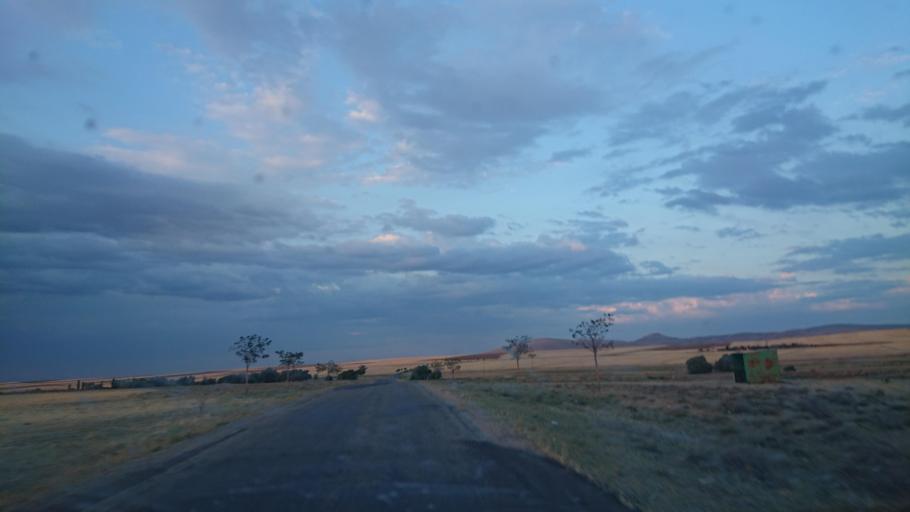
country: TR
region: Aksaray
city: Balci
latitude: 38.8269
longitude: 34.1256
